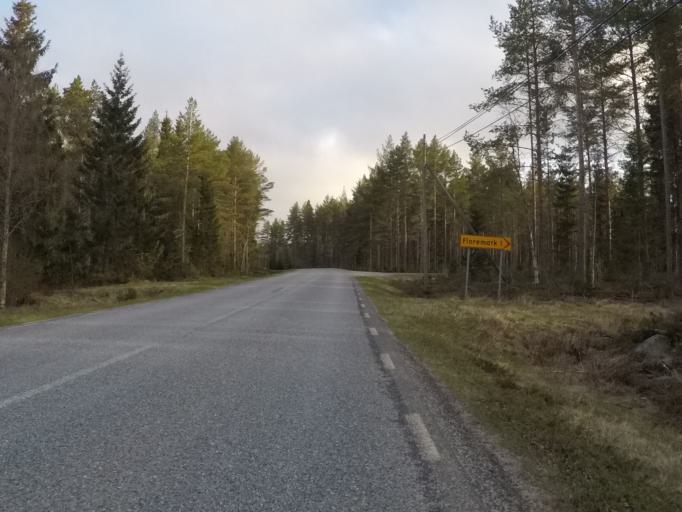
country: SE
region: Vaesterbotten
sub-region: Robertsfors Kommun
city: Robertsfors
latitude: 63.9646
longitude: 20.8101
